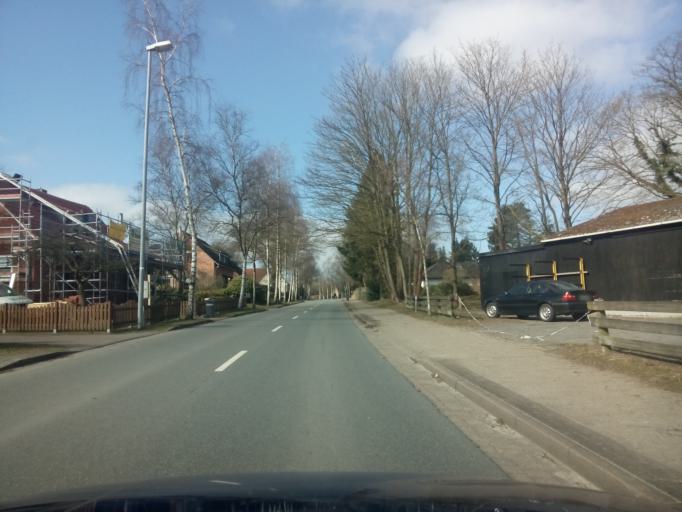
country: DE
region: Lower Saxony
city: Worpswede
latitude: 53.2183
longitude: 8.9419
